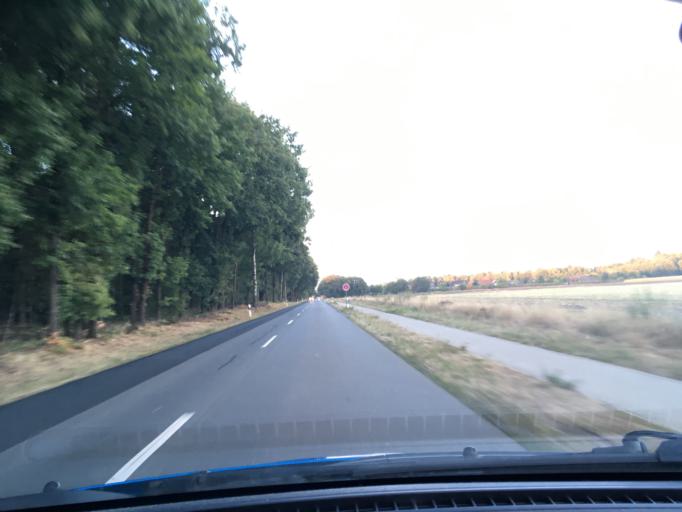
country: DE
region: Lower Saxony
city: Fassberg
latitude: 52.8893
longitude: 10.1482
